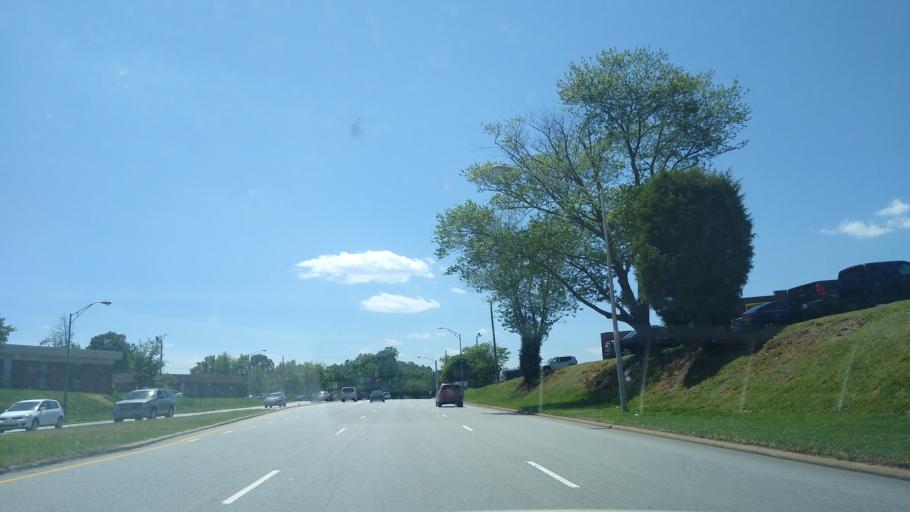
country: US
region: North Carolina
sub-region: Guilford County
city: Greensboro
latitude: 36.0614
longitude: -79.8613
